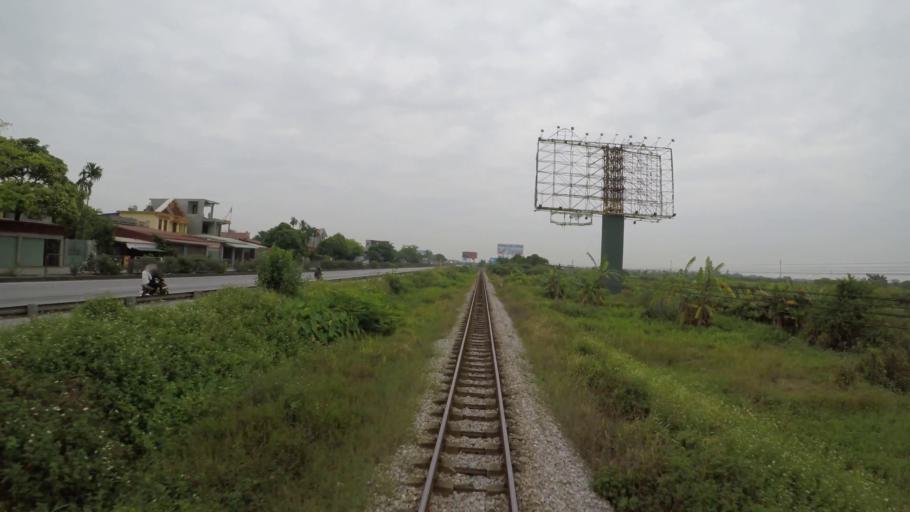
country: VN
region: Hai Duong
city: Phu Thai
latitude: 20.9368
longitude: 106.5490
